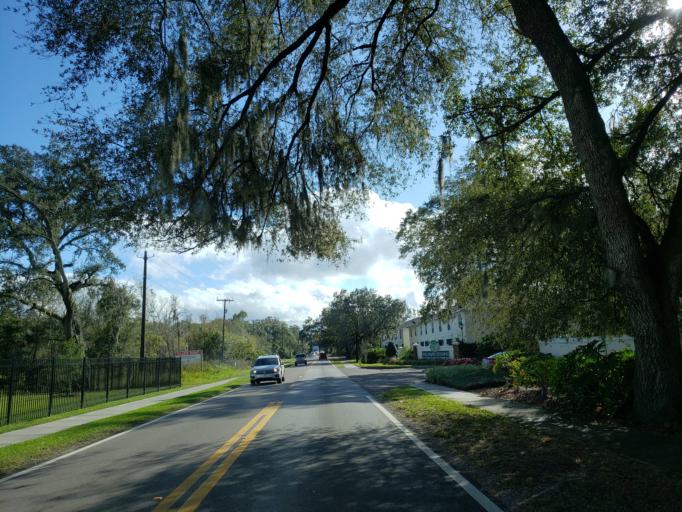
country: US
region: Florida
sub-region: Hillsborough County
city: Mango
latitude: 27.9754
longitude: -82.3187
